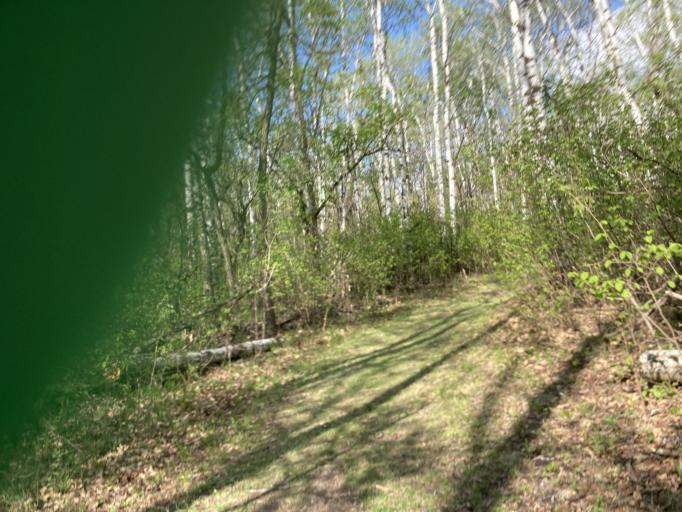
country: CA
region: Manitoba
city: Brandon
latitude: 49.7177
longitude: -99.9025
